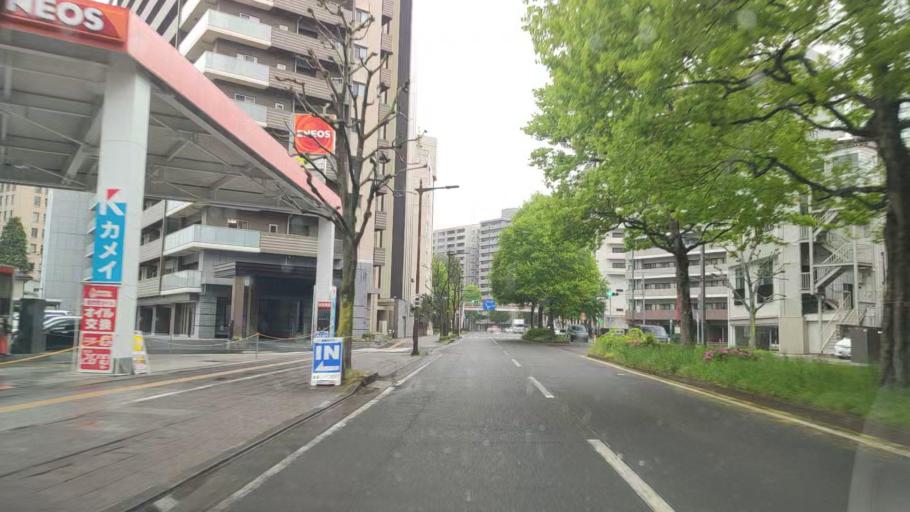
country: JP
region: Miyagi
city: Sendai
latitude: 38.2568
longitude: 140.8712
